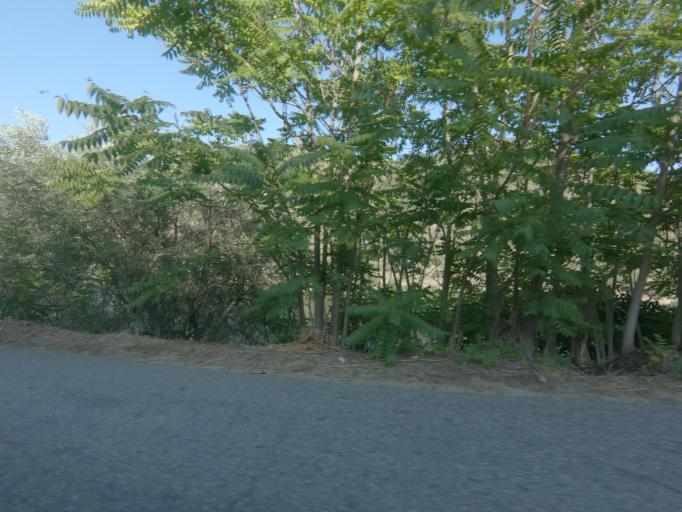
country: PT
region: Vila Real
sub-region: Sabrosa
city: Vilela
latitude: 41.1838
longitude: -7.5522
